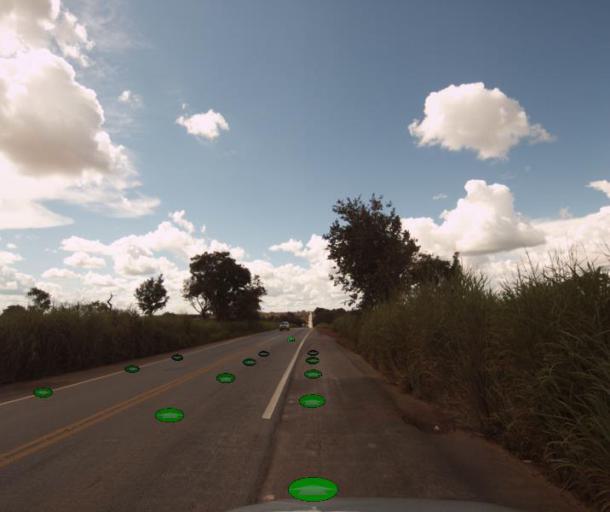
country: BR
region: Goias
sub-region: Porangatu
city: Porangatu
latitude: -13.4810
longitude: -49.1363
